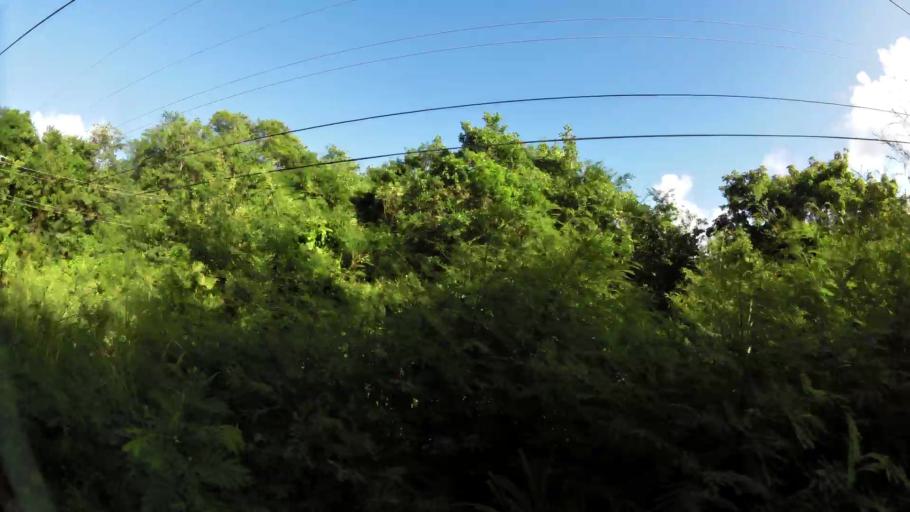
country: LC
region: Gros-Islet
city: Gros Islet
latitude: 14.1019
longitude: -60.9384
